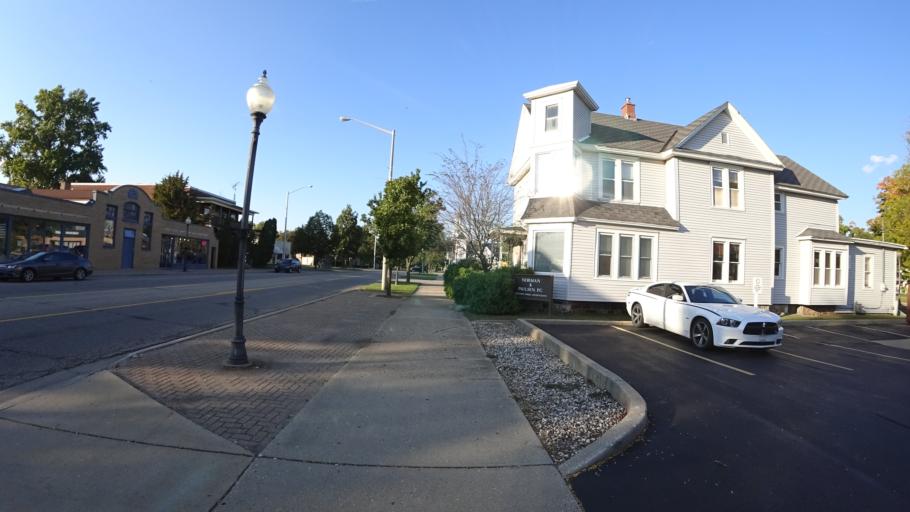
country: US
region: Michigan
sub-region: Saint Joseph County
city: Three Rivers
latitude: 41.9465
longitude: -85.6345
